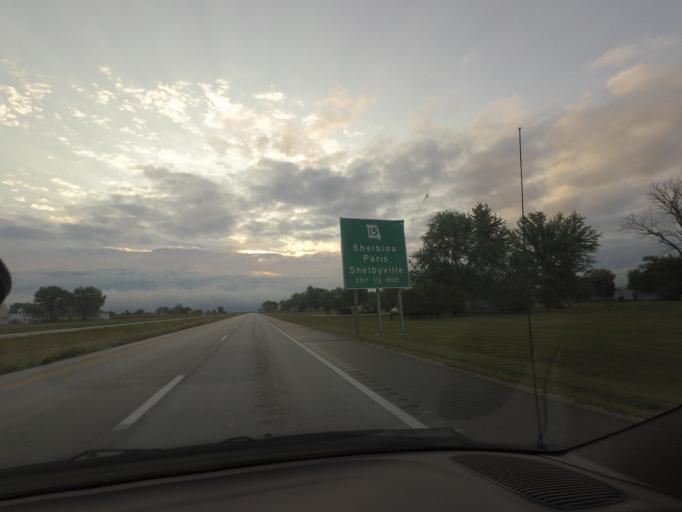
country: US
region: Missouri
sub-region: Shelby County
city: Shelbina
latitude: 39.6980
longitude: -92.0525
